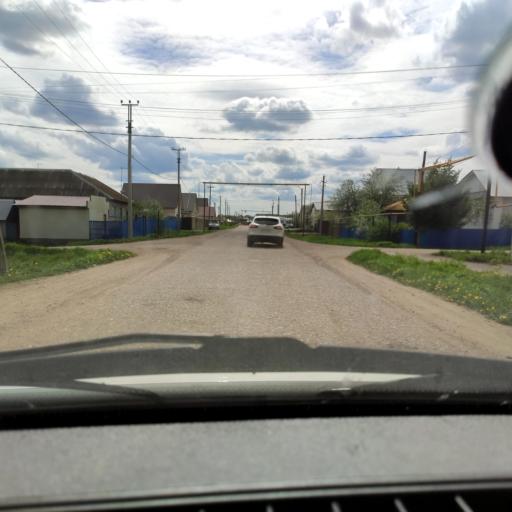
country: RU
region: Bashkortostan
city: Iglino
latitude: 54.8108
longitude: 56.3935
